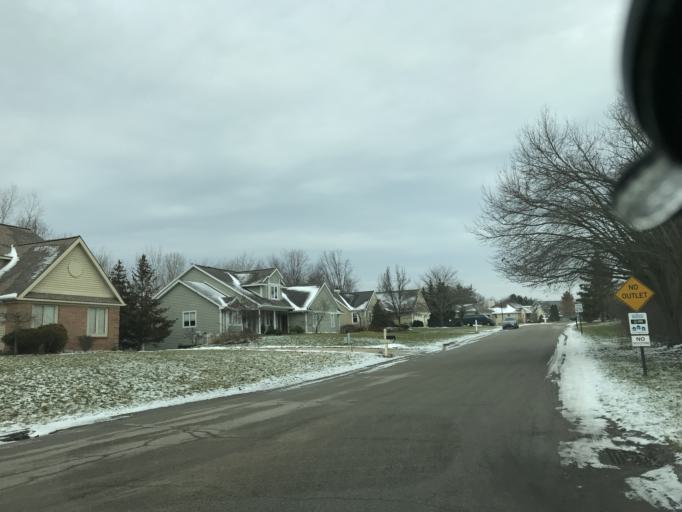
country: US
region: Michigan
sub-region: Kent County
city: East Grand Rapids
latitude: 42.9774
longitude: -85.5795
